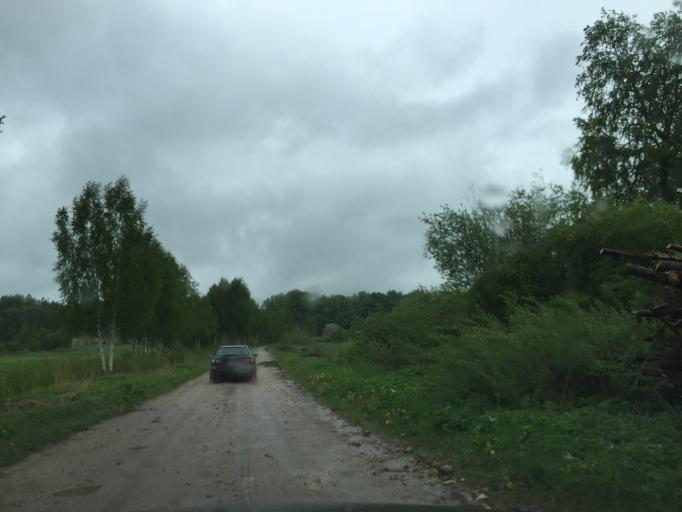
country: LV
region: Ogre
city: Jumprava
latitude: 56.6766
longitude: 25.0124
